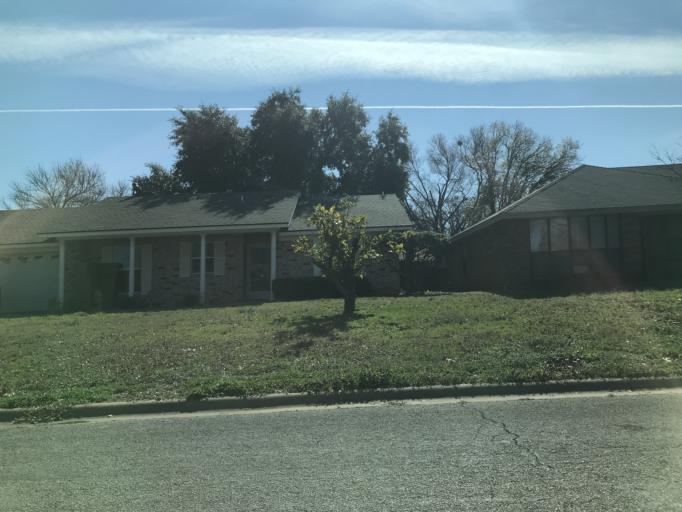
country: US
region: Texas
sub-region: Tom Green County
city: San Angelo
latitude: 31.4354
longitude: -100.4898
